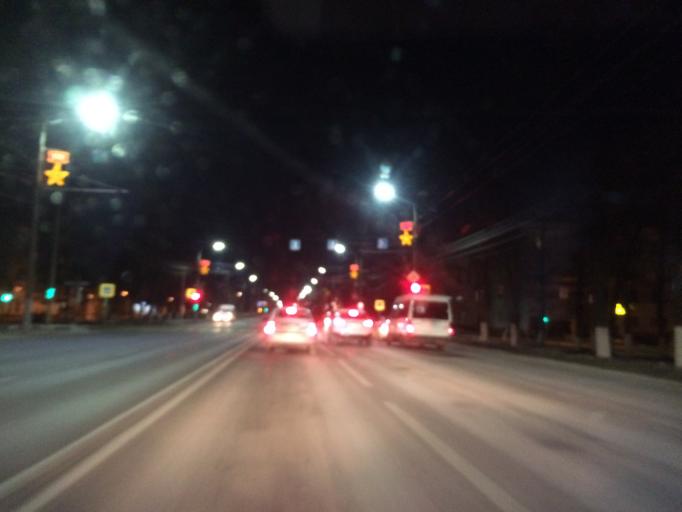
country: RU
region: Tula
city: Tula
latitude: 54.1731
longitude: 37.5956
